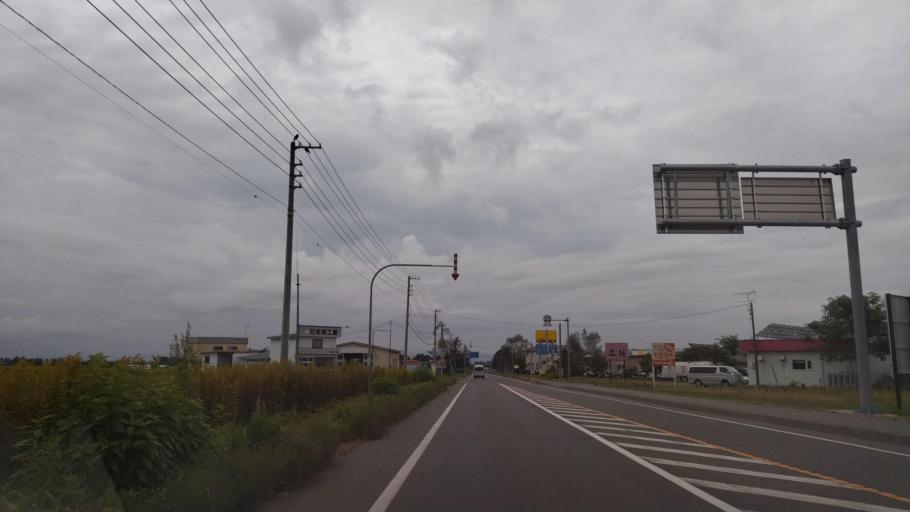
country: JP
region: Hokkaido
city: Otofuke
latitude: 43.2233
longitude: 143.2901
